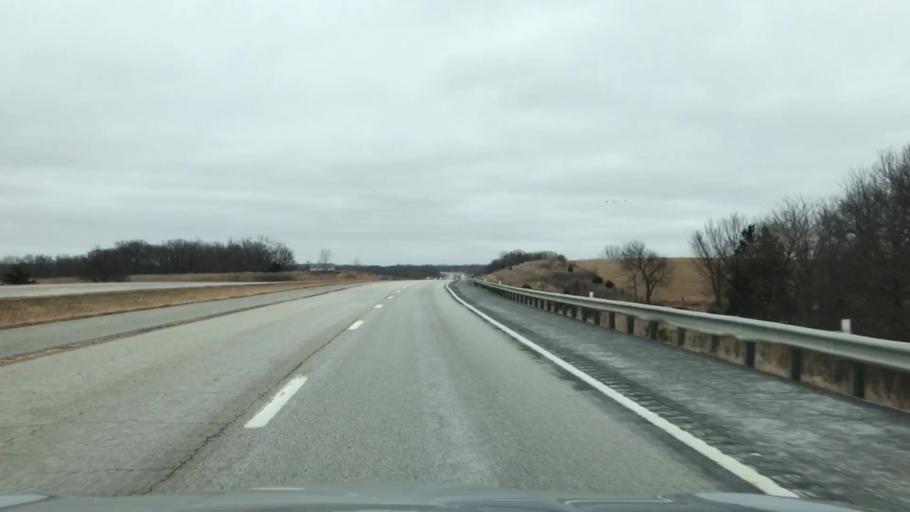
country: US
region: Missouri
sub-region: Caldwell County
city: Hamilton
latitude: 39.7467
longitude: -94.0477
